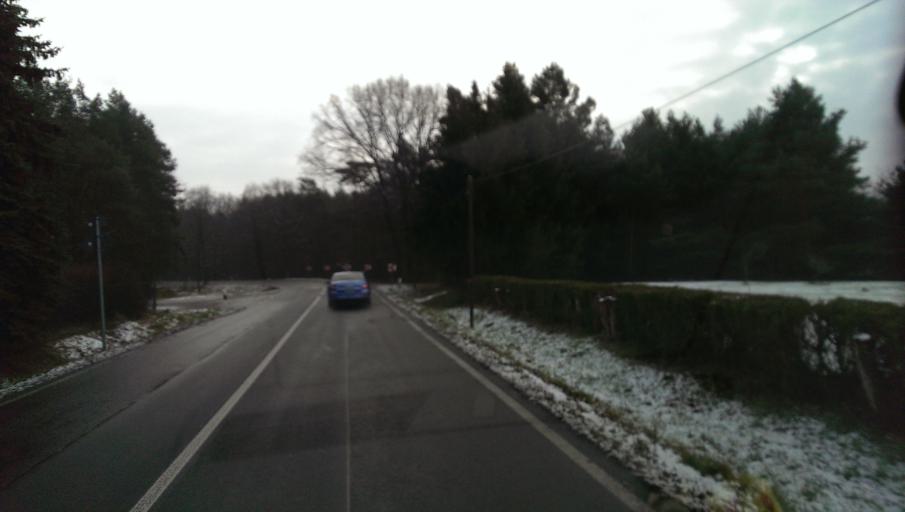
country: DE
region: Brandenburg
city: Merzdorf
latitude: 51.3845
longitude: 13.5129
